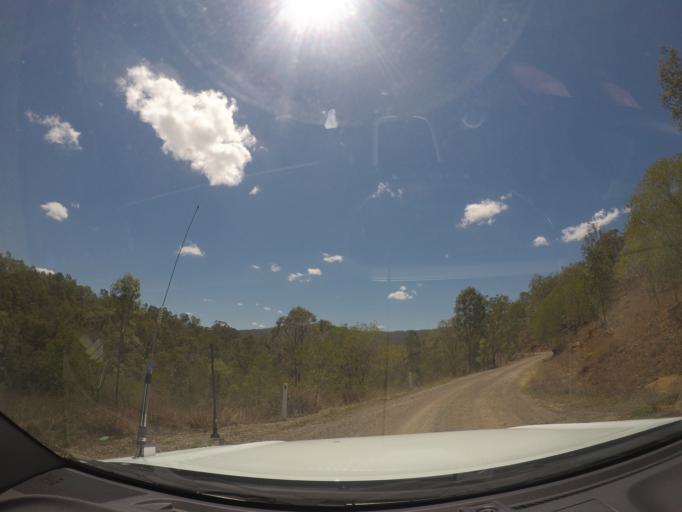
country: AU
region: Queensland
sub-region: Ipswich
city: Springfield Lakes
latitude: -27.8169
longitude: 152.8482
